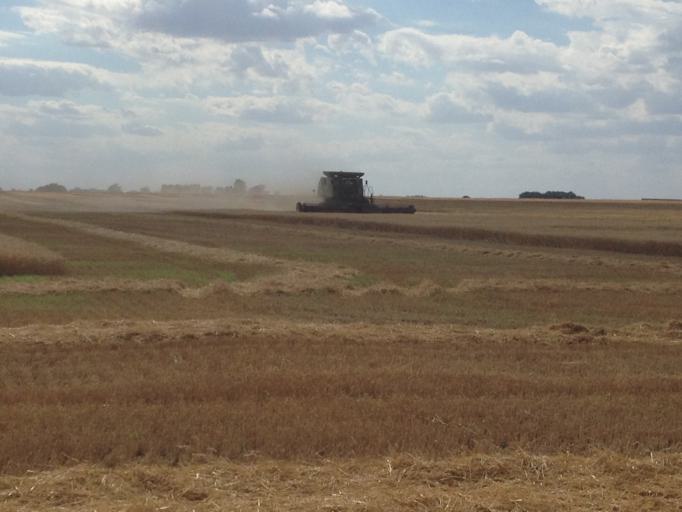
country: US
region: Kansas
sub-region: Stafford County
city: Stafford
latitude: 38.0355
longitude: -98.5825
